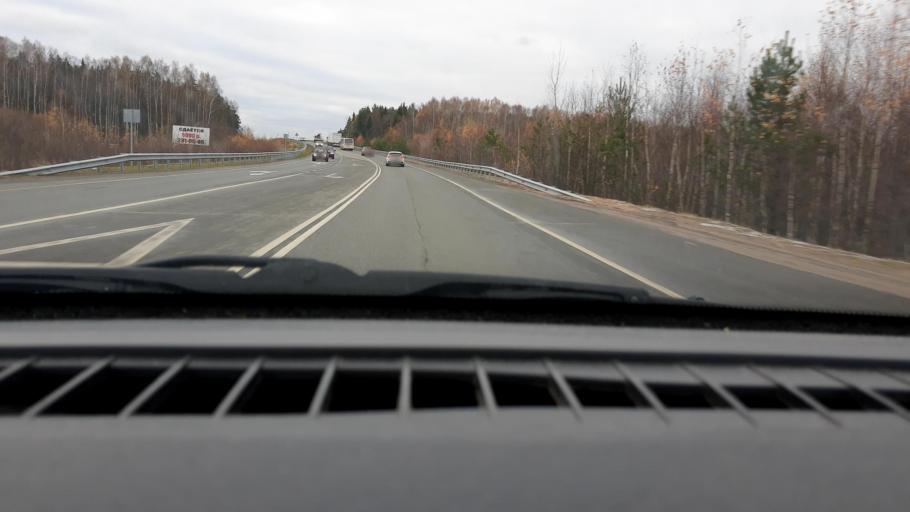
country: RU
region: Nizjnij Novgorod
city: Kstovo
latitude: 56.1592
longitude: 44.1540
